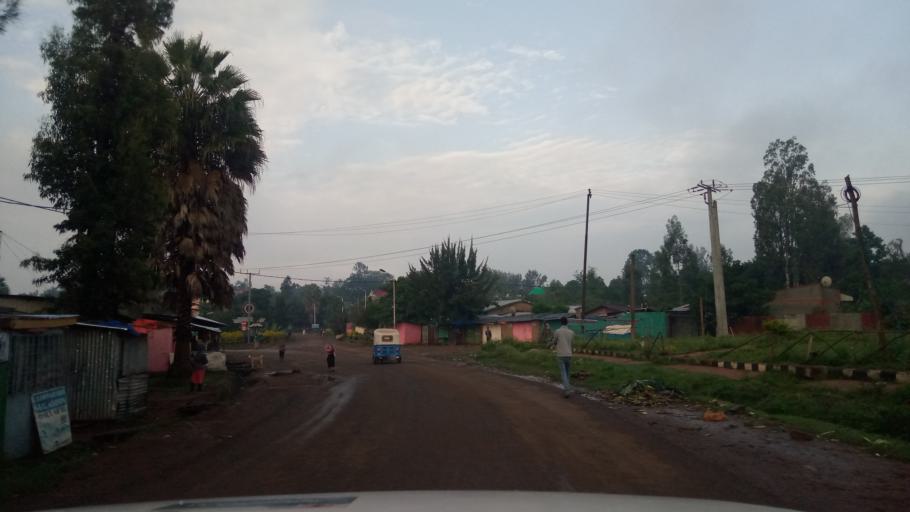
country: ET
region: Oromiya
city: Jima
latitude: 7.6812
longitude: 36.8409
